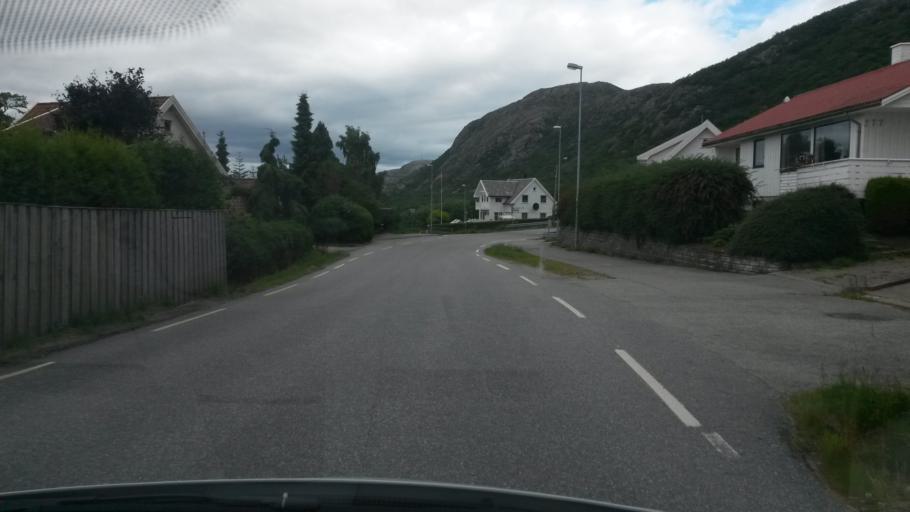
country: NO
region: Rogaland
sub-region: Sandnes
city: Sandnes
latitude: 58.8792
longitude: 5.7738
